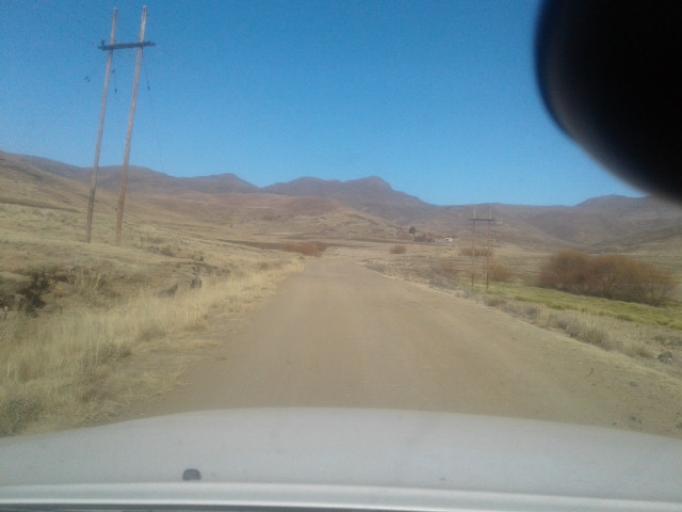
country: LS
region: Maseru
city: Nako
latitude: -29.3759
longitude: 28.0186
